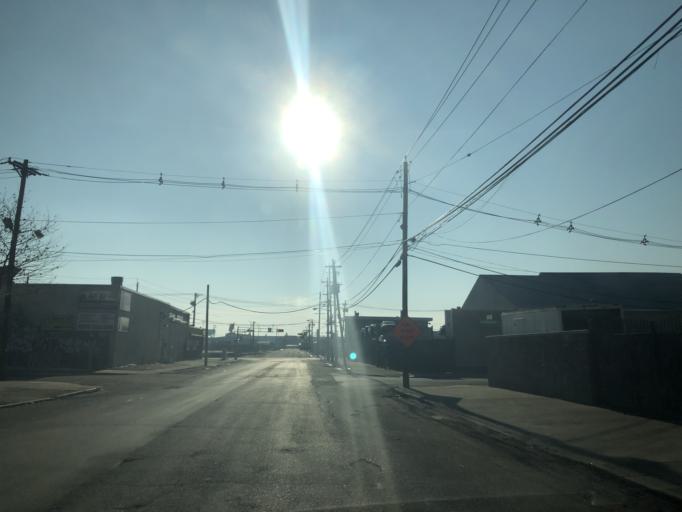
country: US
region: New Jersey
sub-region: Hudson County
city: Harrison
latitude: 40.7210
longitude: -74.1438
